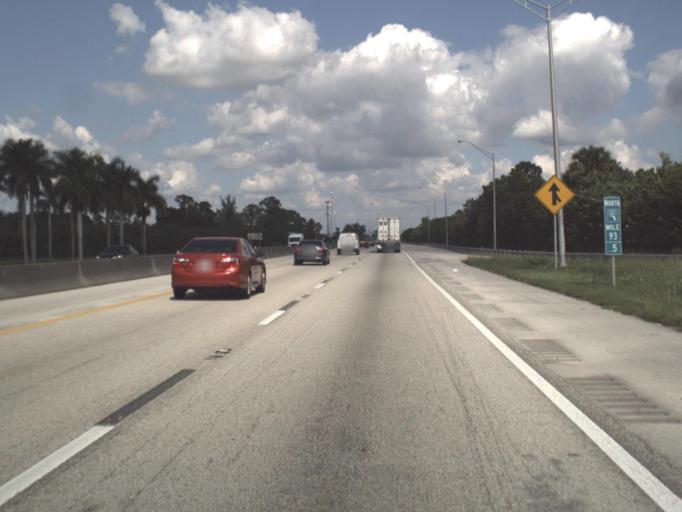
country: US
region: Florida
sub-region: Palm Beach County
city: Greenacres City
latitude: 26.6222
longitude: -80.1737
